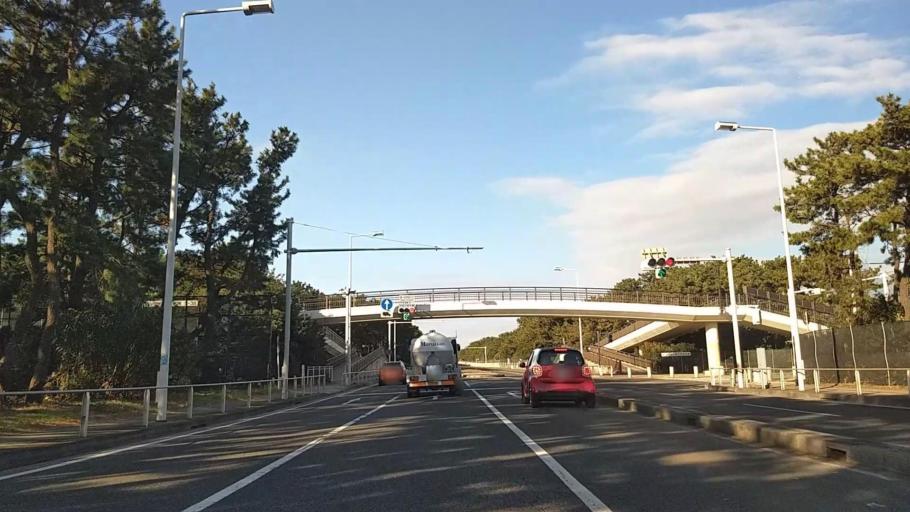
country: JP
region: Kanagawa
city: Chigasaki
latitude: 35.3180
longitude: 139.4158
